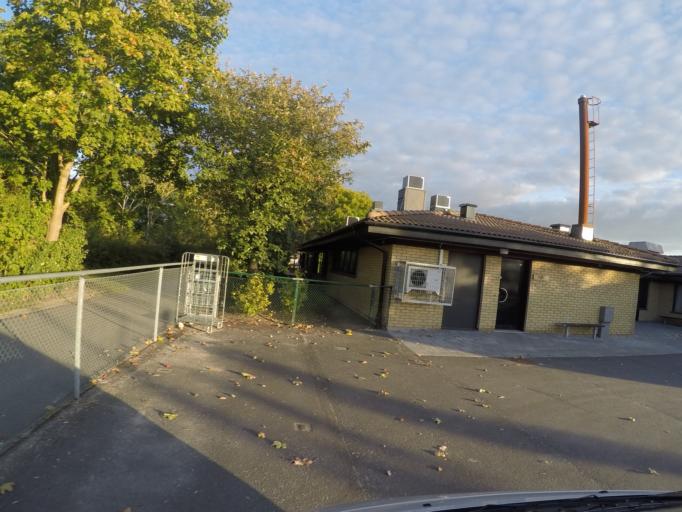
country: SE
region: Skane
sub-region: Lunds Kommun
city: Genarp
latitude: 55.6719
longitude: 13.3397
